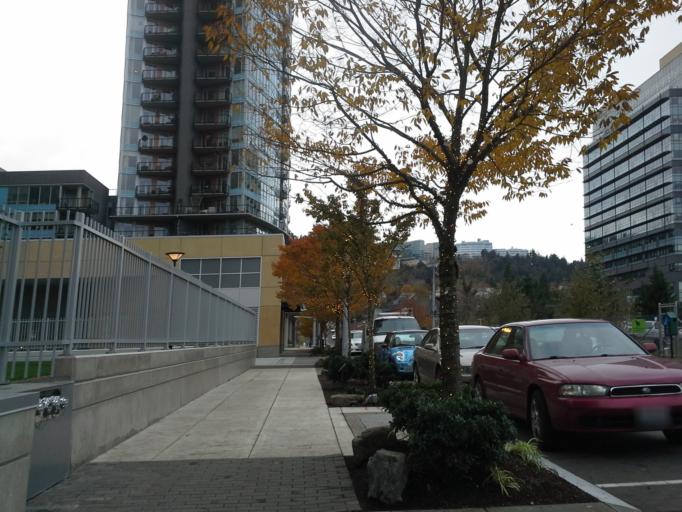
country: US
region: Oregon
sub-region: Multnomah County
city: Portland
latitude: 45.4978
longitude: -122.6690
